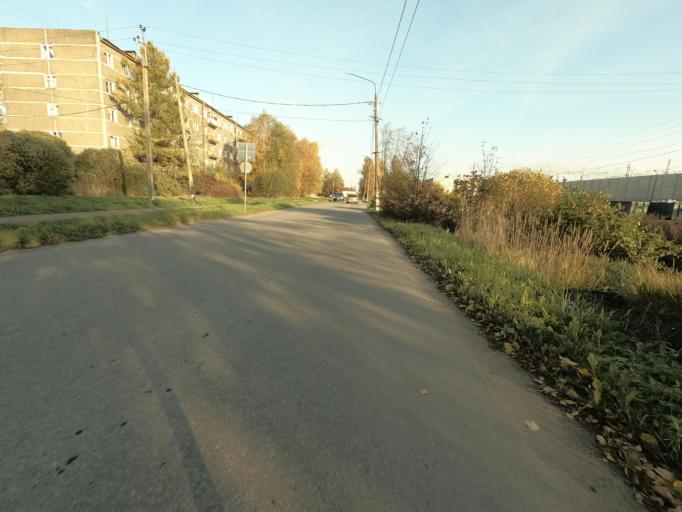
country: RU
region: Leningrad
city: Mga
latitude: 59.7574
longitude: 31.0532
